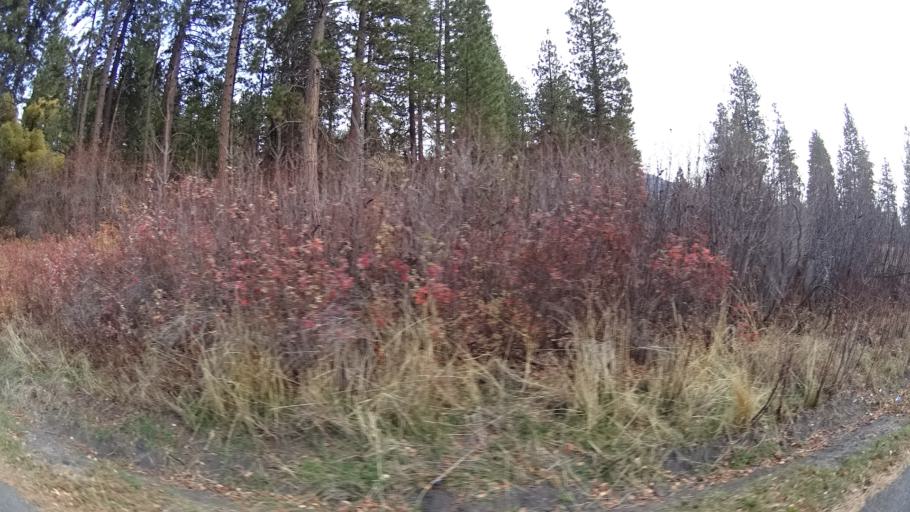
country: US
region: California
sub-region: Siskiyou County
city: Weed
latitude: 41.4400
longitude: -122.3766
